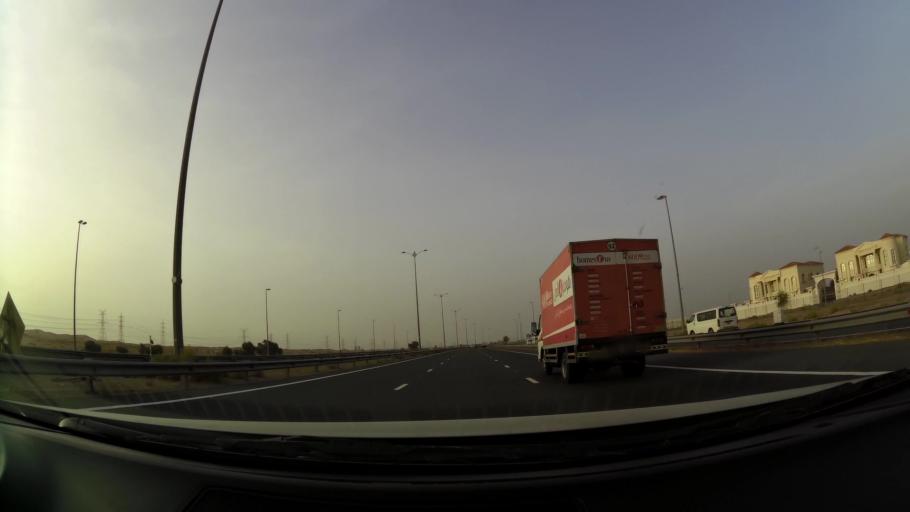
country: OM
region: Al Buraimi
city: Al Buraymi
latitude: 24.2936
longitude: 55.7377
